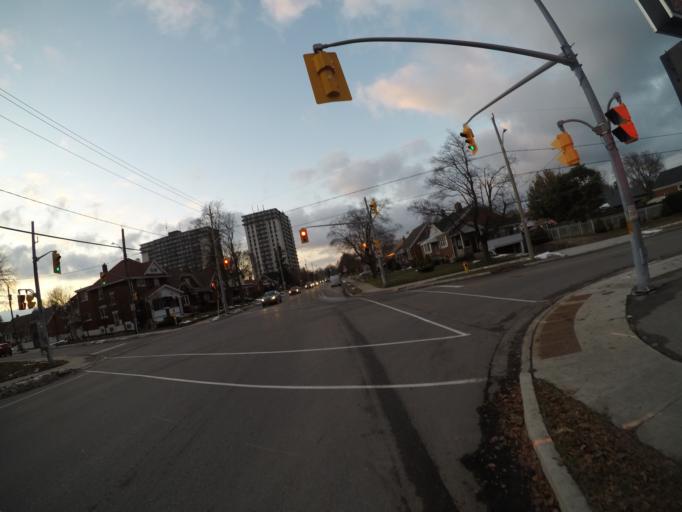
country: CA
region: Ontario
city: Waterloo
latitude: 43.4630
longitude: -80.4940
